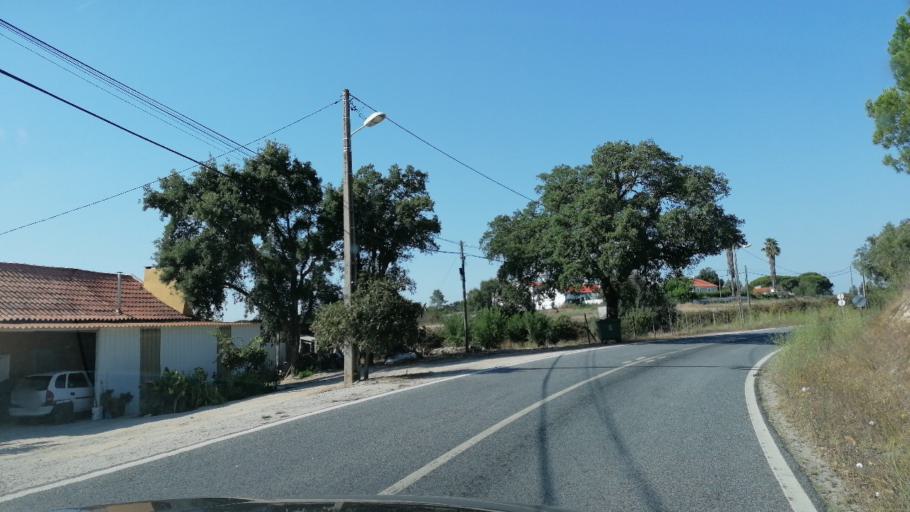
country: PT
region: Santarem
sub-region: Benavente
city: Poceirao
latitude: 38.7608
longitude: -8.6324
